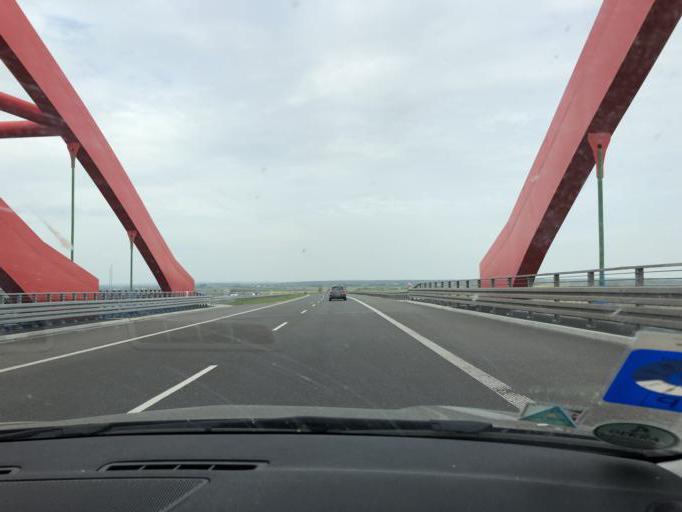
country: PL
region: Subcarpathian Voivodeship
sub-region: Powiat przeworski
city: Rozborz
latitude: 50.0636
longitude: 22.5648
